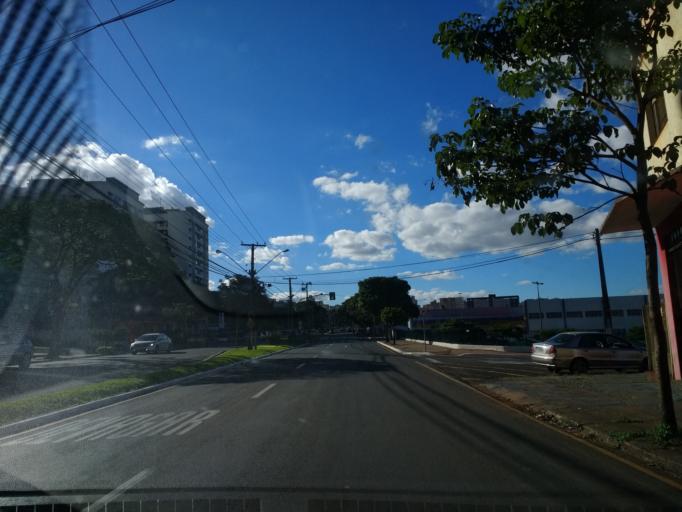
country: BR
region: Parana
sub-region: Londrina
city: Londrina
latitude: -23.3314
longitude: -51.1519
